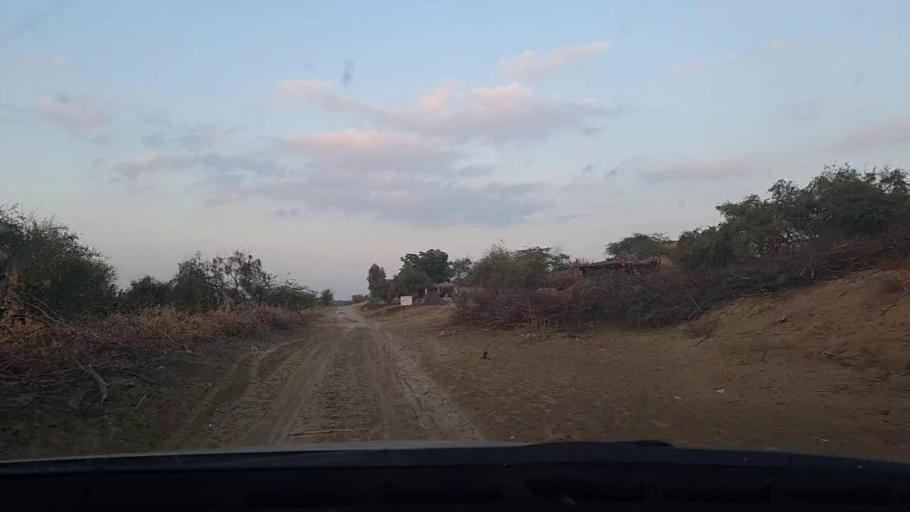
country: PK
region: Sindh
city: Tando Mittha Khan
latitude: 25.9486
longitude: 69.3395
